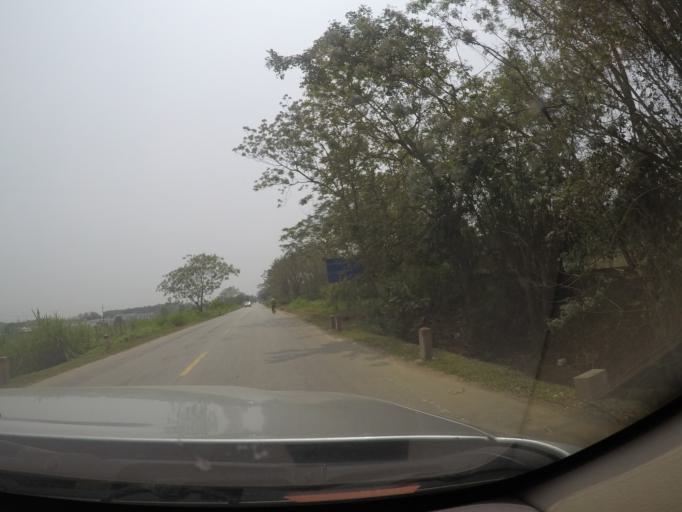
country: VN
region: Thanh Hoa
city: Thi Tran Thuong Xuan
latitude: 19.9906
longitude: 105.4040
